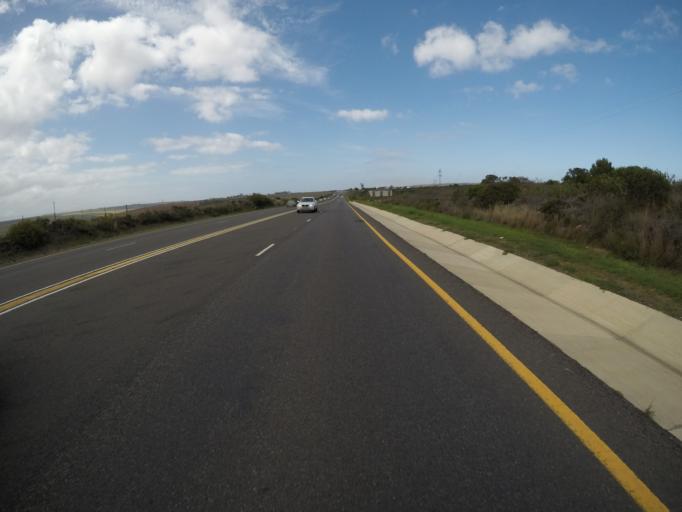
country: ZA
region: Western Cape
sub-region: Eden District Municipality
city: Mossel Bay
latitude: -34.1811
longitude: 22.0310
